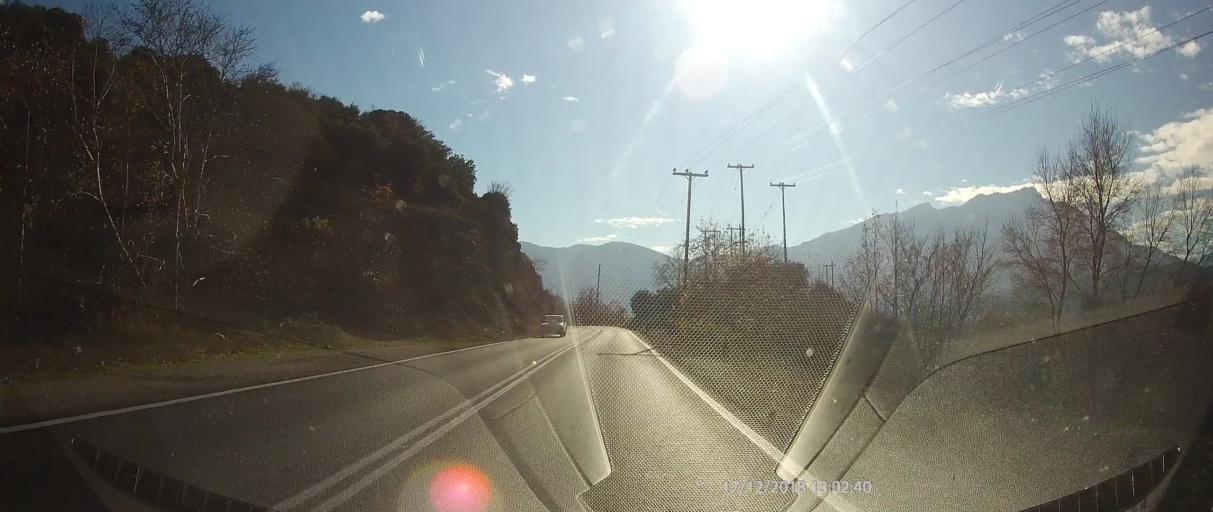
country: GR
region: Thessaly
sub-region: Trikala
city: Kastraki
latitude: 39.7205
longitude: 21.5949
